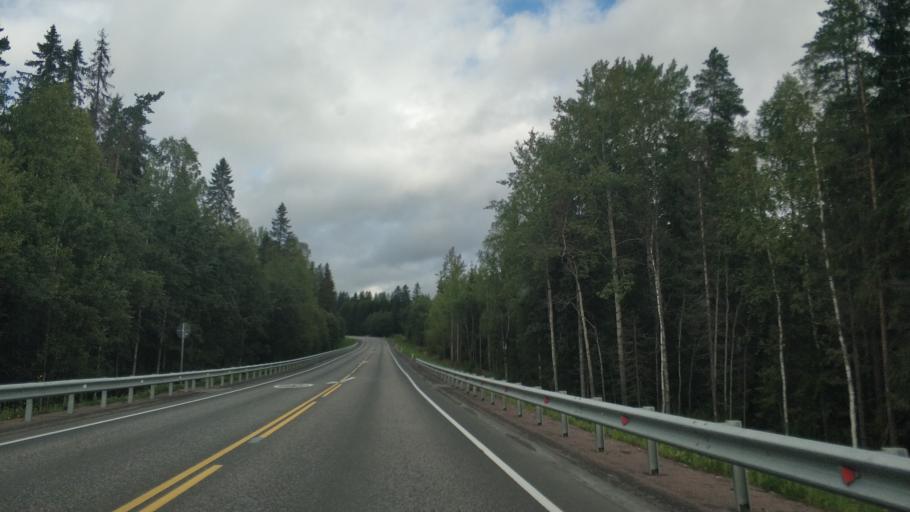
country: RU
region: Republic of Karelia
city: Khelyulya
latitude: 61.7892
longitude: 30.6325
